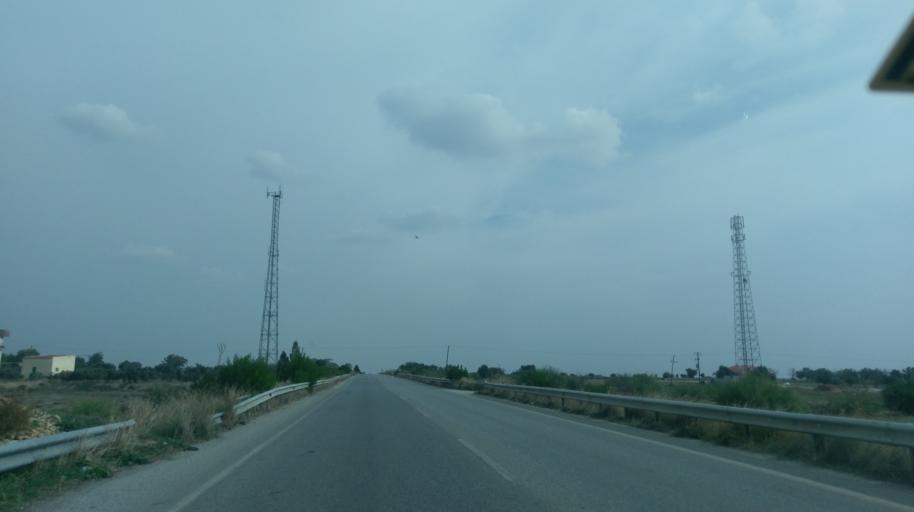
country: CY
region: Ammochostos
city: Lefkonoiko
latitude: 35.2596
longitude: 33.6611
